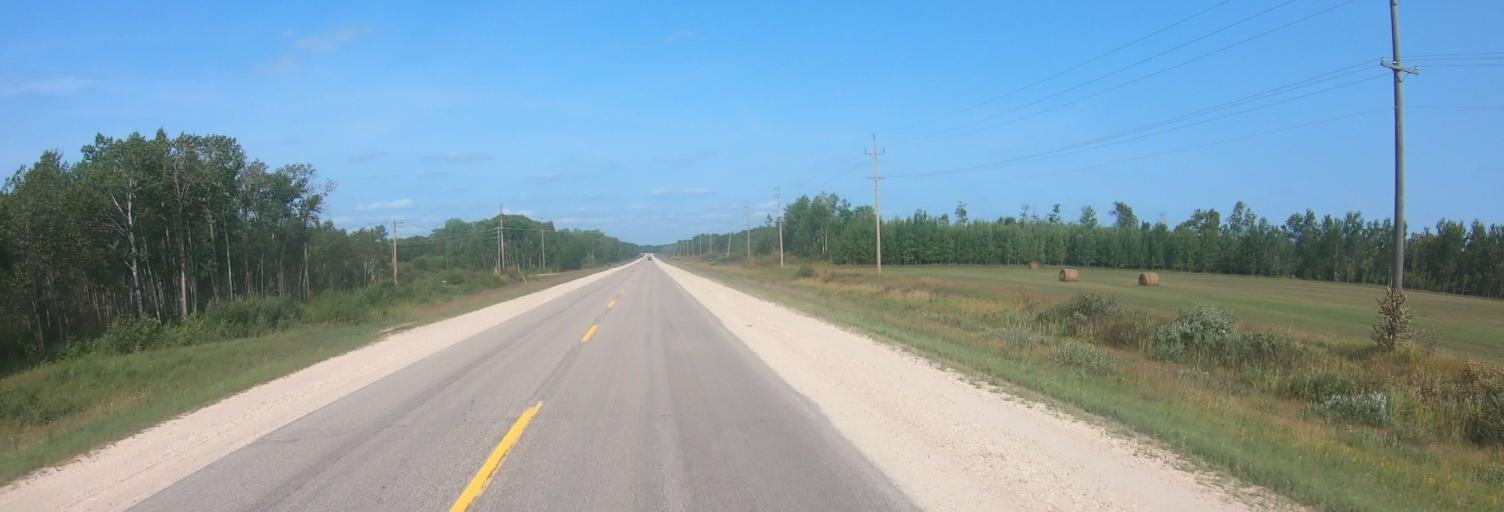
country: US
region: Minnesota
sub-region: Roseau County
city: Roseau
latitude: 49.1635
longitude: -96.1438
